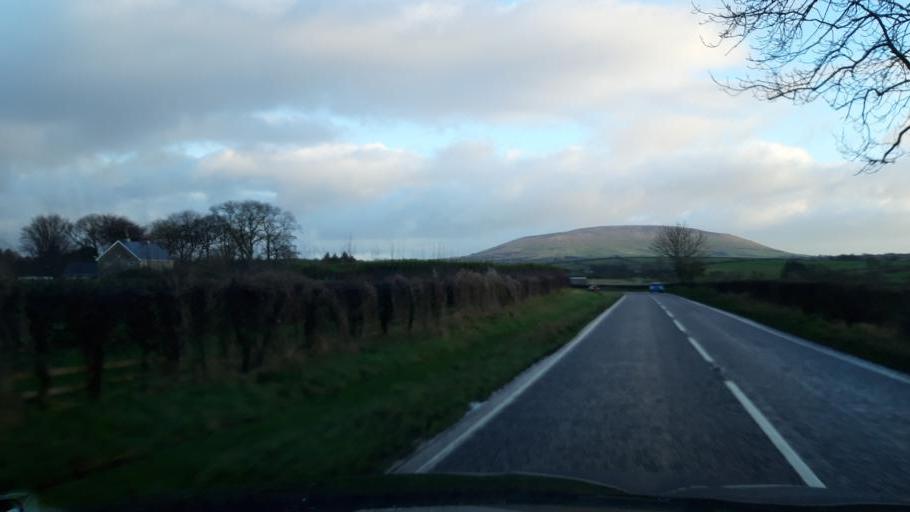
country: GB
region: Northern Ireland
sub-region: Moyle District
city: Ballycastle
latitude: 55.1206
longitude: -6.3261
